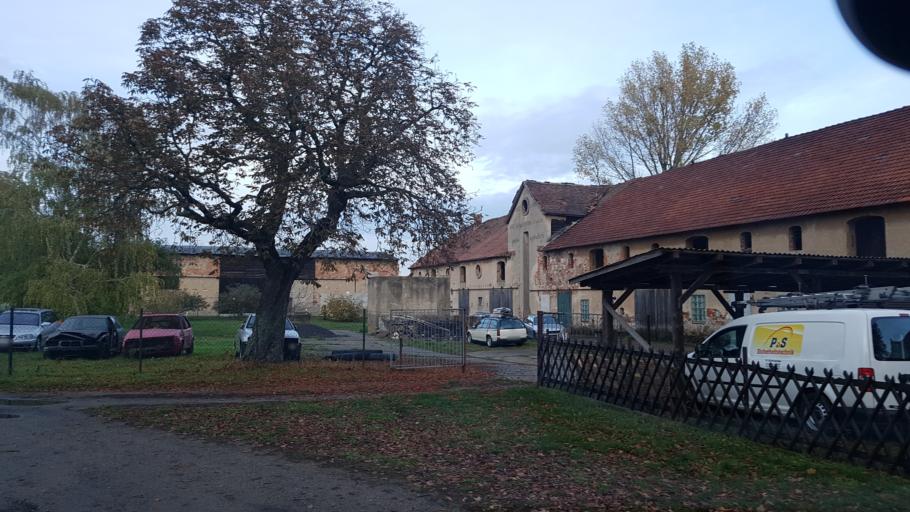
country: DE
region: Brandenburg
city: Falkenberg
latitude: 51.5368
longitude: 13.2273
